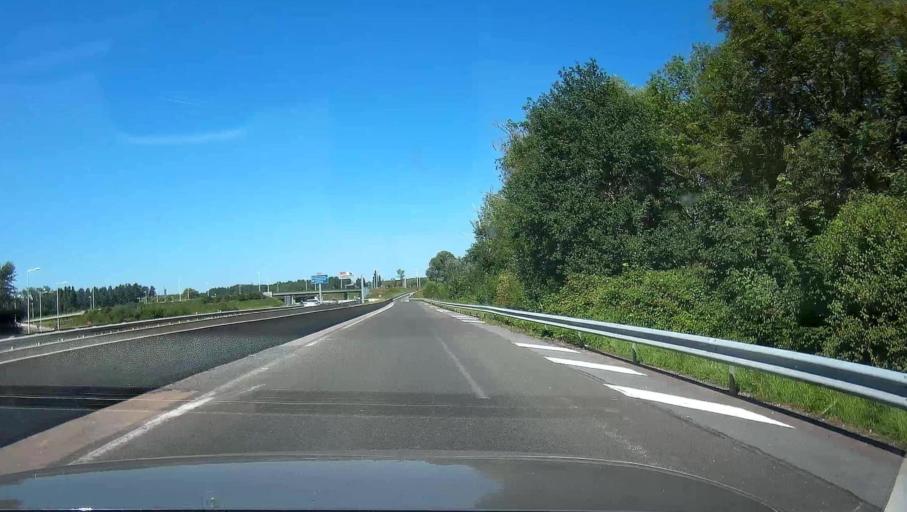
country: FR
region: Champagne-Ardenne
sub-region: Departement de la Marne
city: Cormontreuil
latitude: 49.2202
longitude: 4.0700
